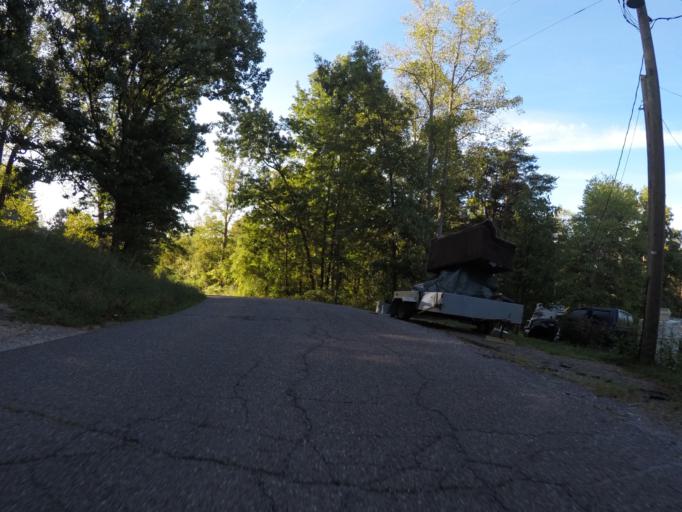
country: US
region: Ohio
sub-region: Lawrence County
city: Coal Grove
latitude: 38.5866
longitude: -82.5524
